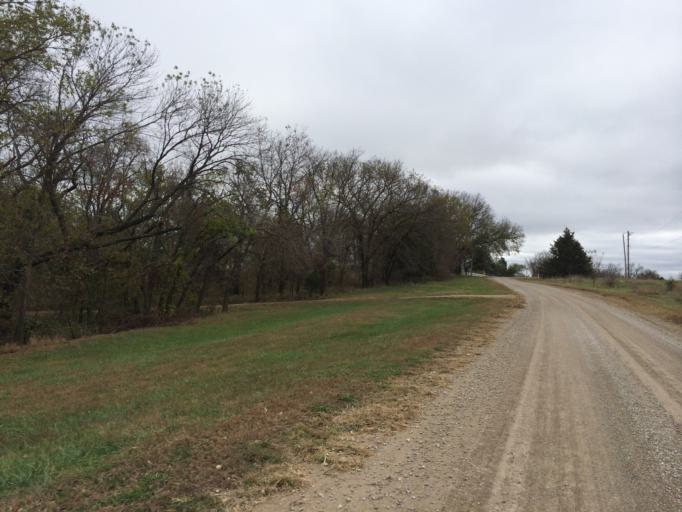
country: US
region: Kansas
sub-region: Douglas County
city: Lawrence
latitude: 38.8959
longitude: -95.3354
